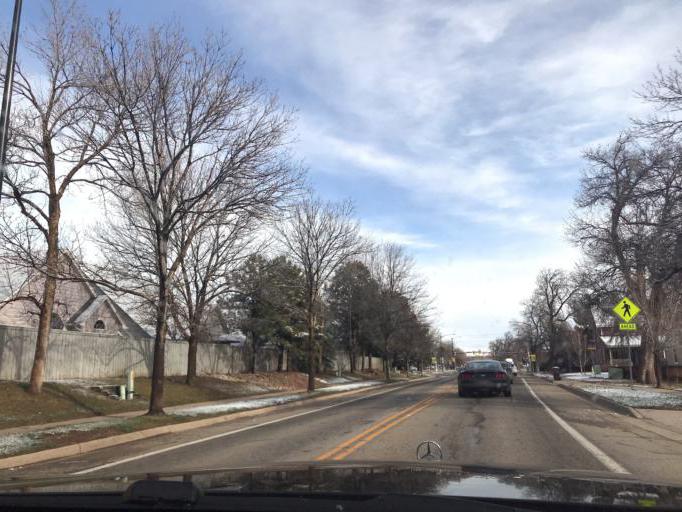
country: US
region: Colorado
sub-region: Boulder County
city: Boulder
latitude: 40.0123
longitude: -105.2254
